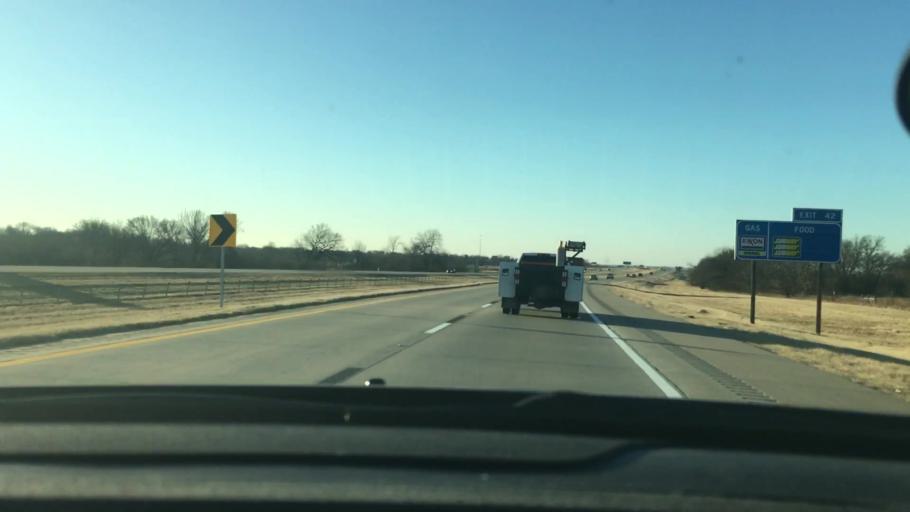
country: US
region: Oklahoma
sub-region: Murray County
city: Davis
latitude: 34.3437
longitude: -97.1484
